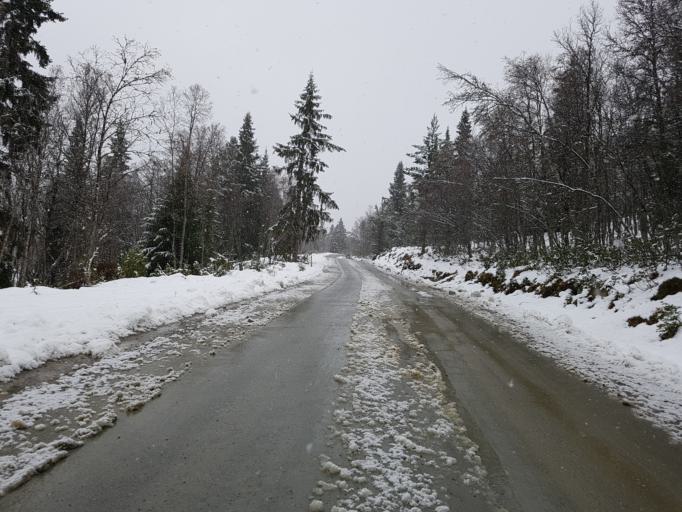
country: NO
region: Oppland
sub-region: Sel
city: Otta
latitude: 61.7927
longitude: 9.7177
